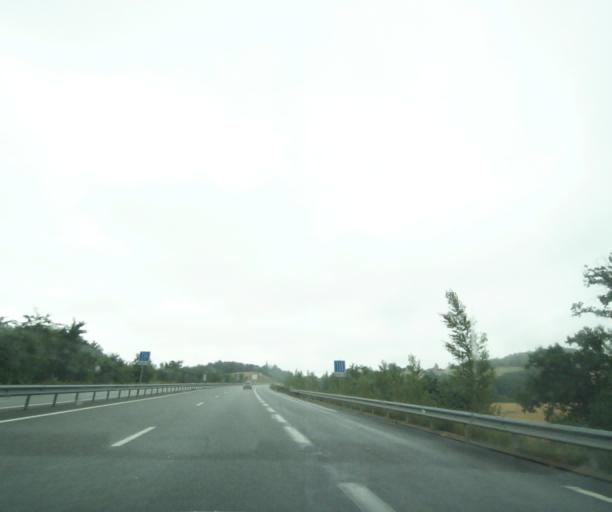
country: FR
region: Midi-Pyrenees
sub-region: Departement du Tarn
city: Le Garric
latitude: 44.0009
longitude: 2.1719
